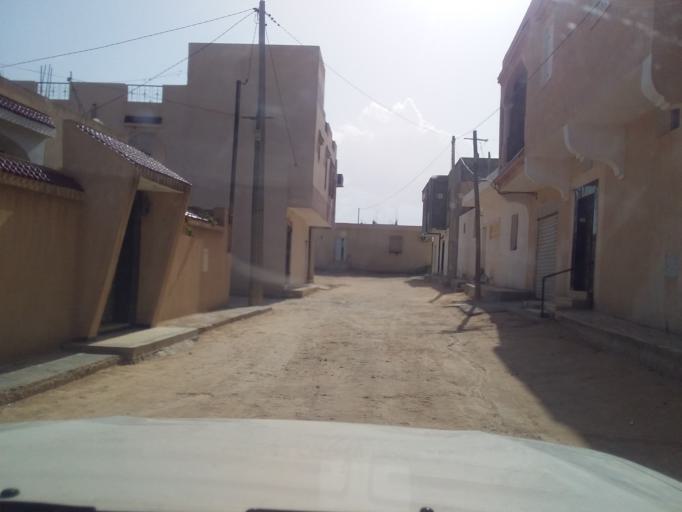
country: TN
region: Qabis
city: Gabes
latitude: 33.6414
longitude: 10.2972
